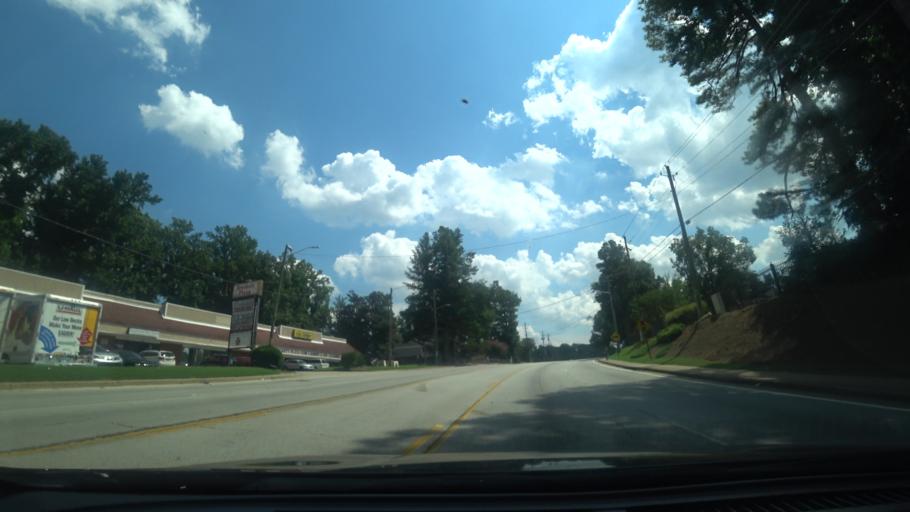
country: US
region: Georgia
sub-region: DeKalb County
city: Clarkston
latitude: 33.8214
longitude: -84.2317
